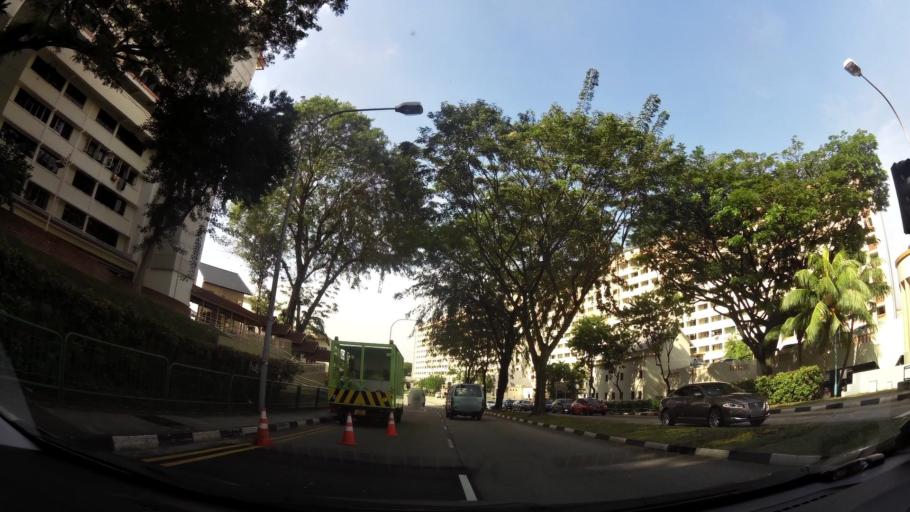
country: SG
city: Singapore
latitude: 1.3552
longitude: 103.8371
